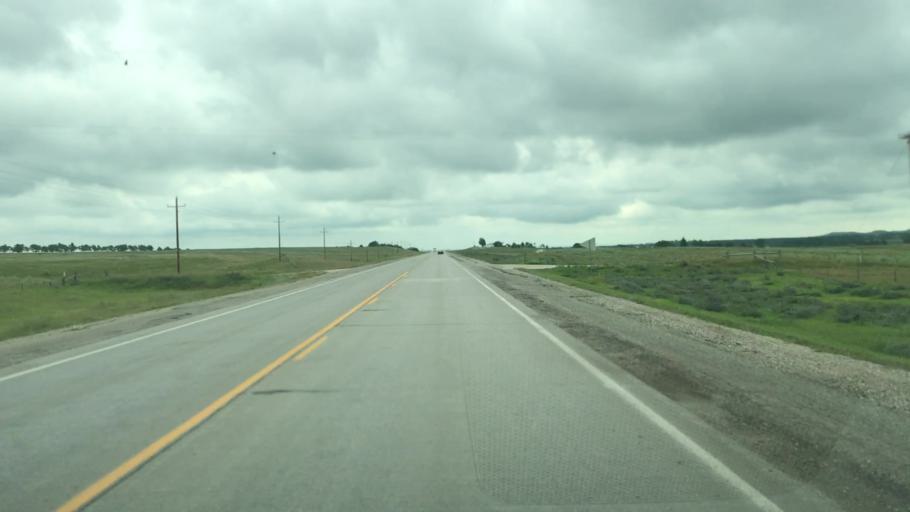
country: US
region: South Dakota
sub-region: Todd County
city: Mission
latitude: 43.3029
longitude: -100.7065
